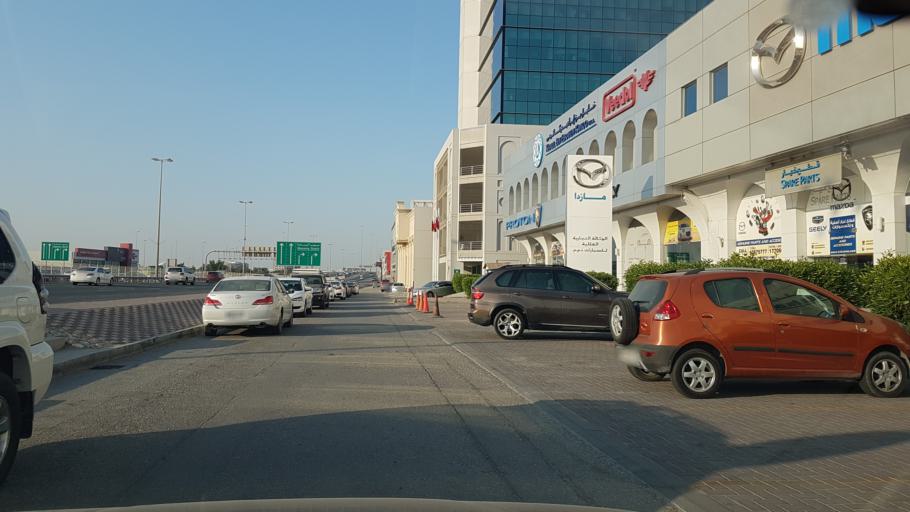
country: BH
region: Northern
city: Madinat `Isa
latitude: 26.1892
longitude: 50.5362
